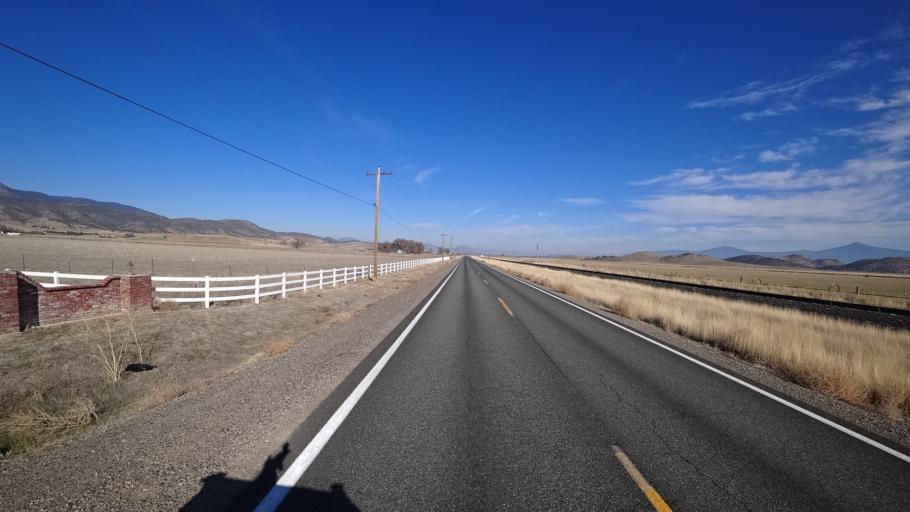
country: US
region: California
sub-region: Siskiyou County
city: Montague
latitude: 41.5692
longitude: -122.5253
